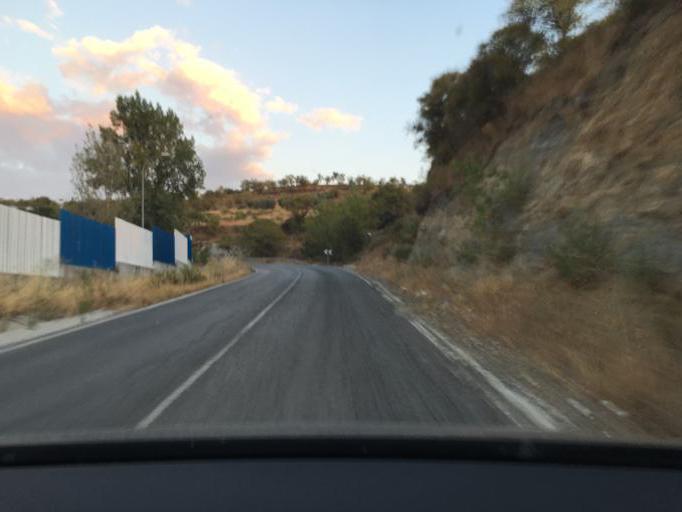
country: ES
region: Andalusia
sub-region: Provincia de Granada
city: Beas de Granada
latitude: 37.2268
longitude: -3.4938
